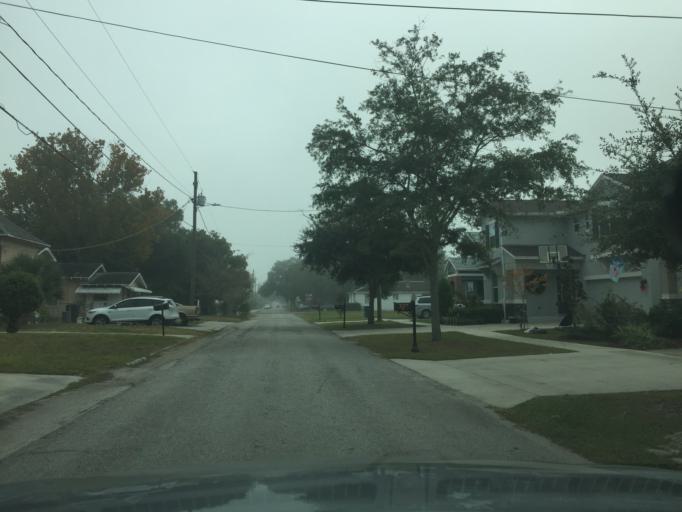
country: US
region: Florida
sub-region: Hillsborough County
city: Tampa
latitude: 27.9485
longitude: -82.4862
